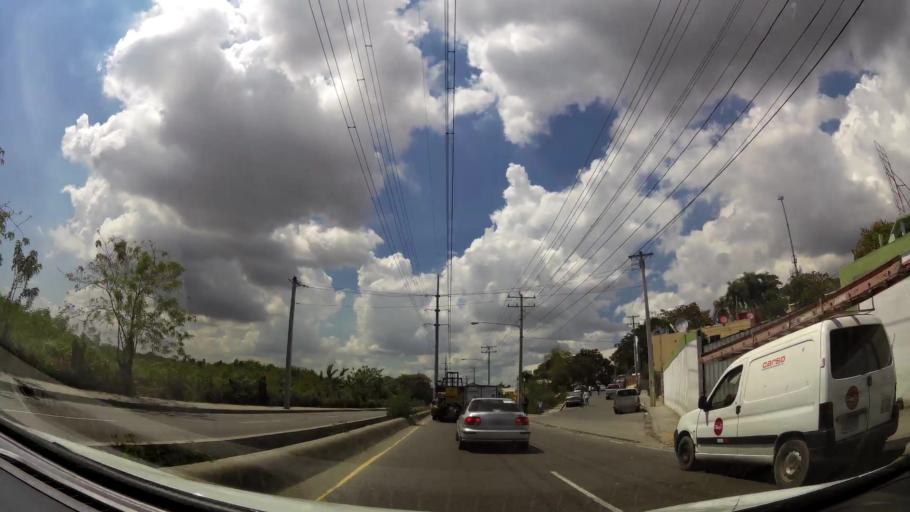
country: DO
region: Nacional
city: Santo Domingo
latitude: 18.5078
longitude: -69.9620
